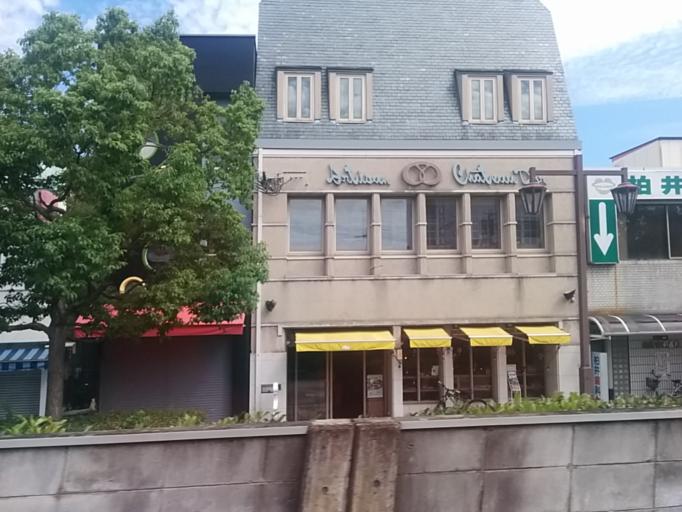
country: JP
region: Nara
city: Kashihara-shi
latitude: 34.5091
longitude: 135.7908
